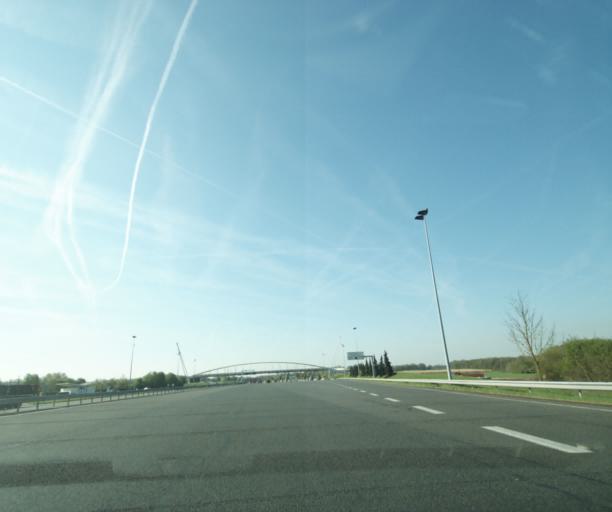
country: FR
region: Ile-de-France
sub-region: Departement de Seine-et-Marne
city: Souppes-sur-Loing
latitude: 48.1787
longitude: 2.7668
